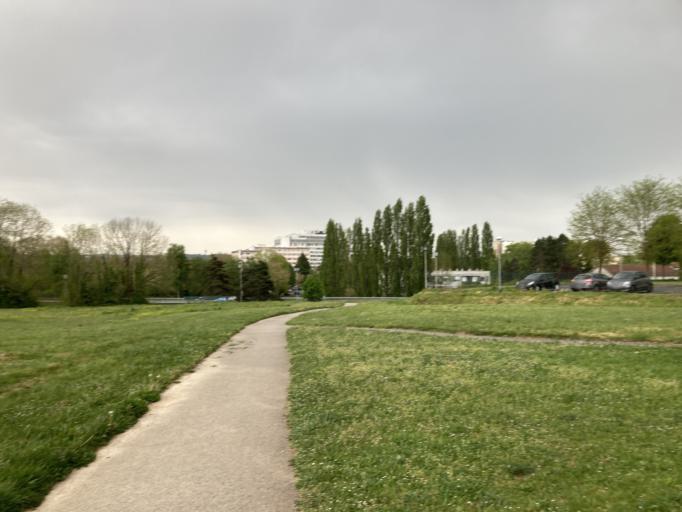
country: FR
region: Limousin
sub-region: Departement de la Haute-Vienne
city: Isle
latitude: 45.8158
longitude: 1.2303
